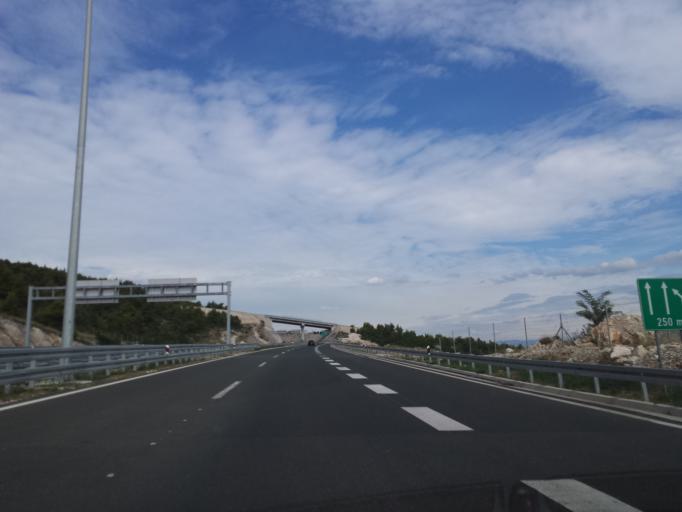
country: BA
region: Federation of Bosnia and Herzegovina
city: Ljubuski
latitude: 43.1534
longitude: 17.4808
